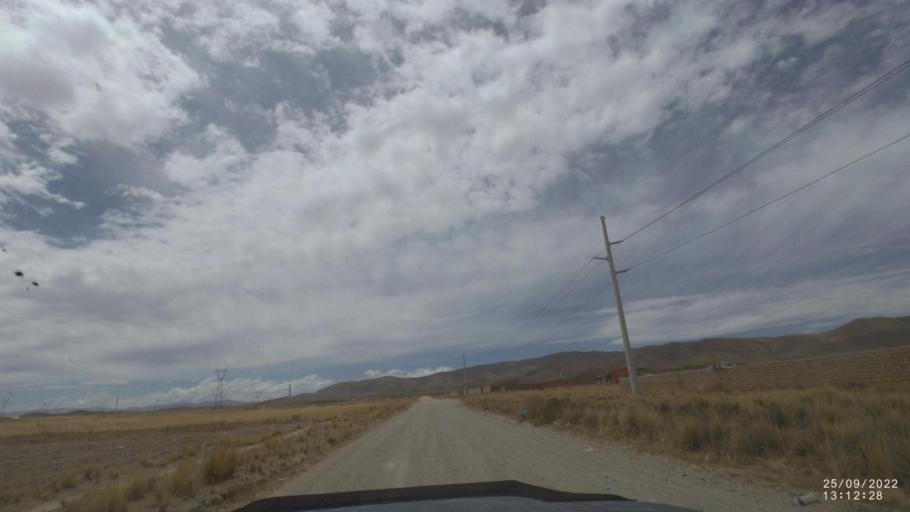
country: BO
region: Oruro
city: Oruro
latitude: -17.9569
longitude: -67.0410
